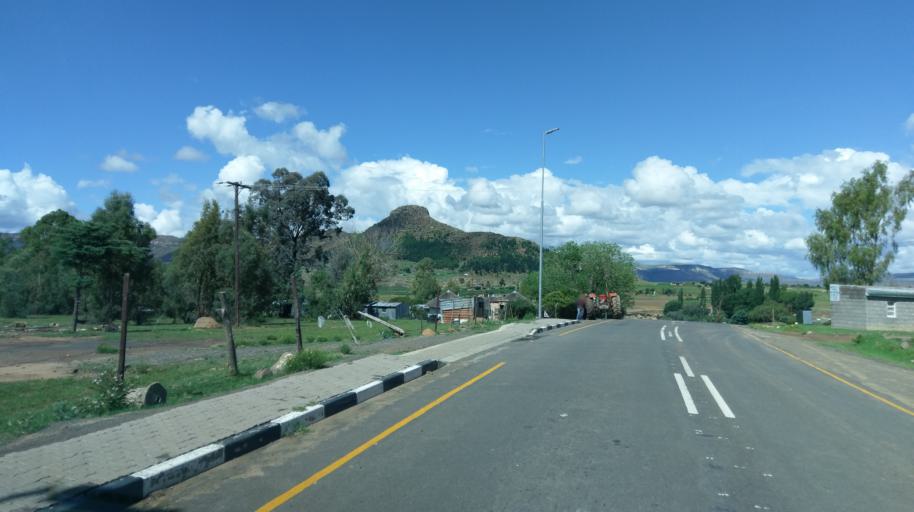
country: LS
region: Mafeteng
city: Mafeteng
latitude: -29.6934
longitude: 27.4407
